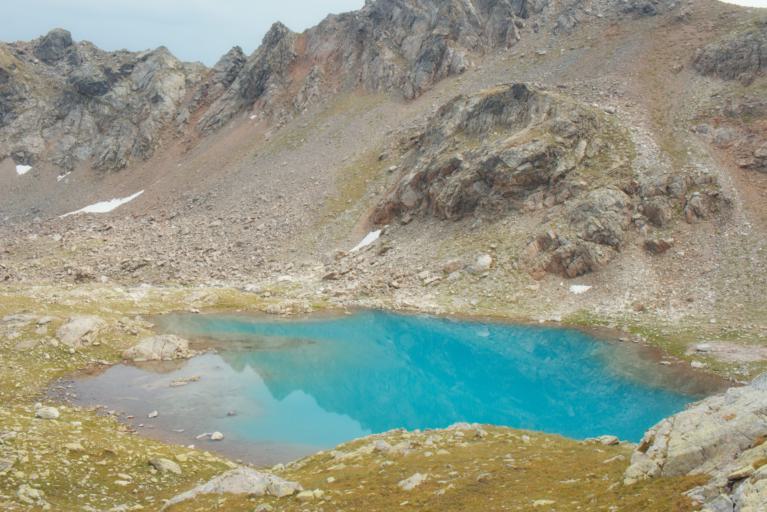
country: RU
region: Karachayevo-Cherkesiya
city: Nizhniy Arkhyz
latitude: 43.4515
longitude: 41.2328
